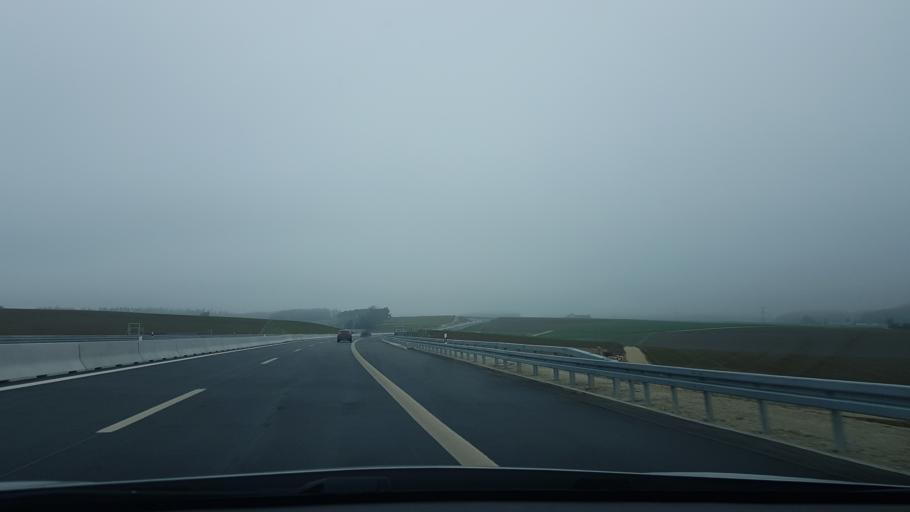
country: DE
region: Bavaria
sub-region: Lower Bavaria
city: Essenbach
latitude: 48.6308
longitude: 12.2078
